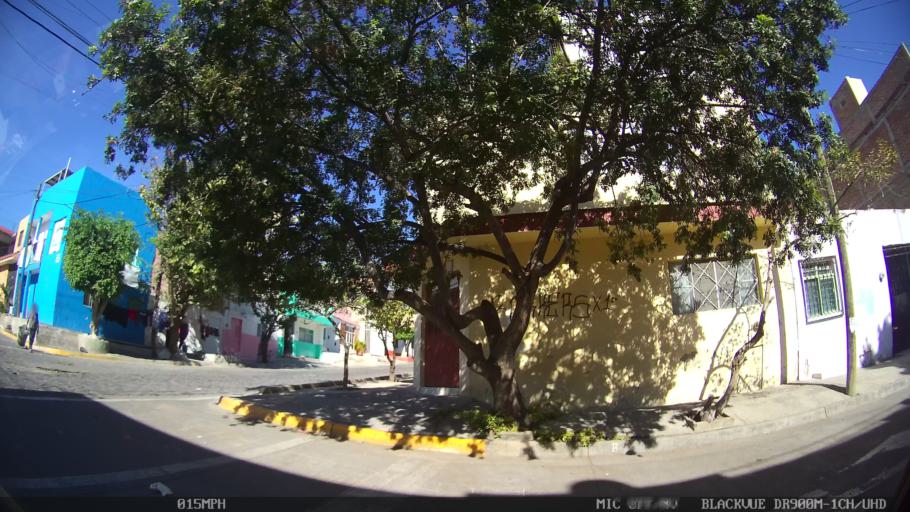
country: MX
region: Jalisco
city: Tlaquepaque
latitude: 20.6869
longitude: -103.2727
